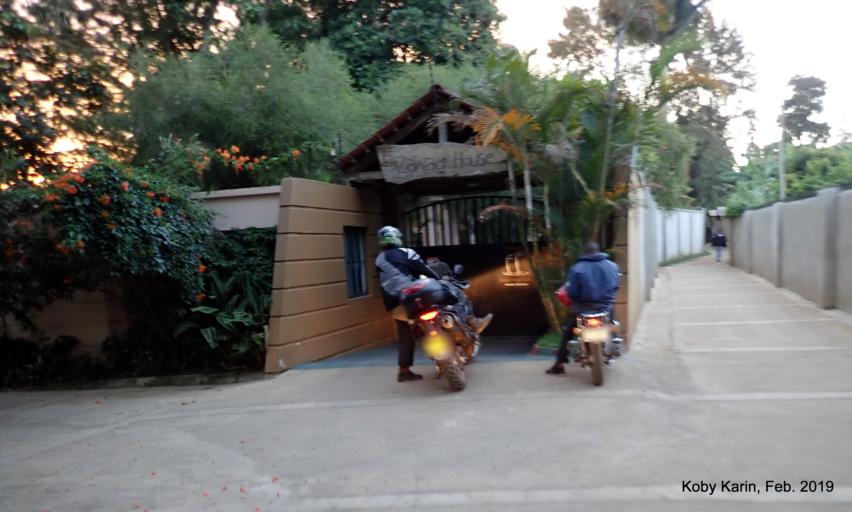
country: TZ
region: Arusha
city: Arusha
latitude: -3.3653
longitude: 36.7144
